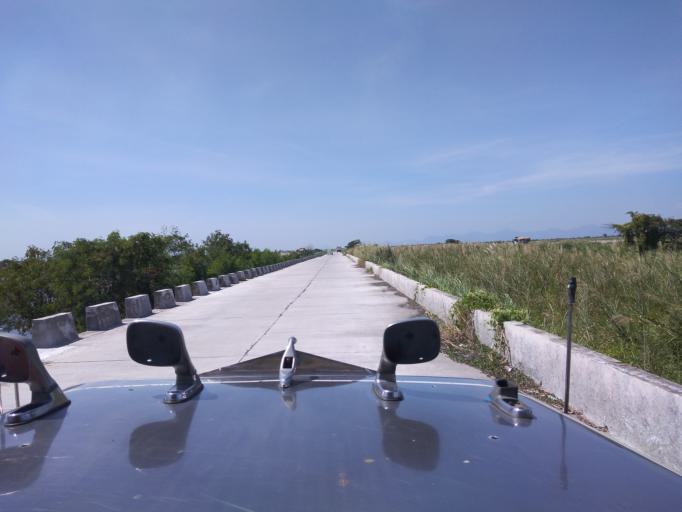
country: PH
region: Central Luzon
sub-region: Province of Pampanga
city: Minalin
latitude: 14.9814
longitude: 120.6866
